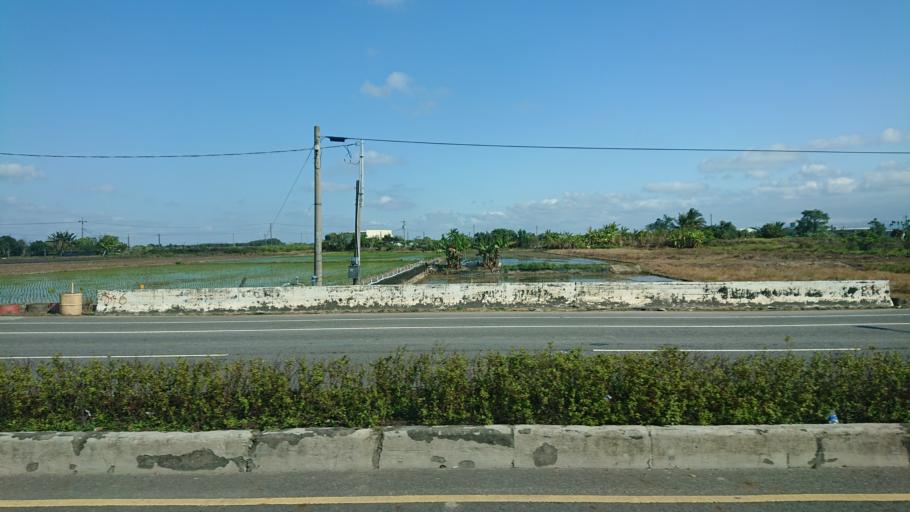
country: TW
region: Taiwan
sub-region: Chiayi
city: Taibao
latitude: 23.4404
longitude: 120.3809
